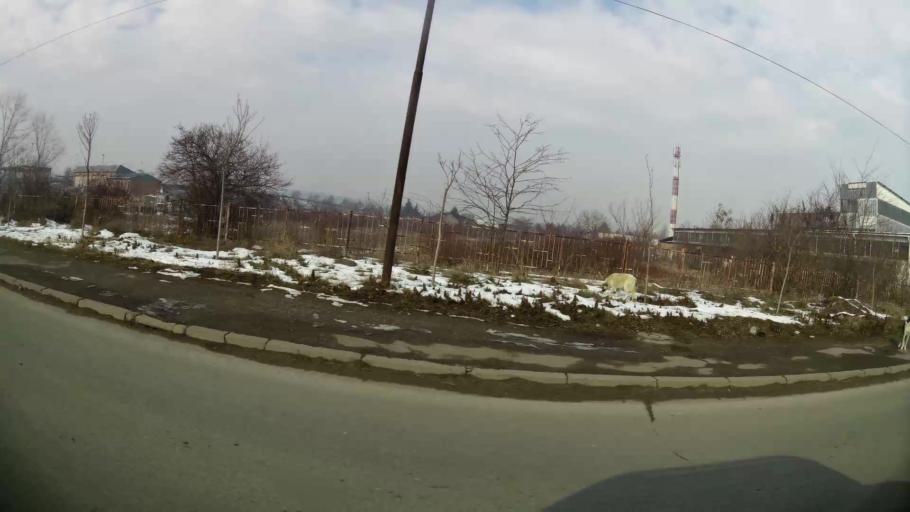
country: MK
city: Krushopek
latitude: 42.0129
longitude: 21.3618
